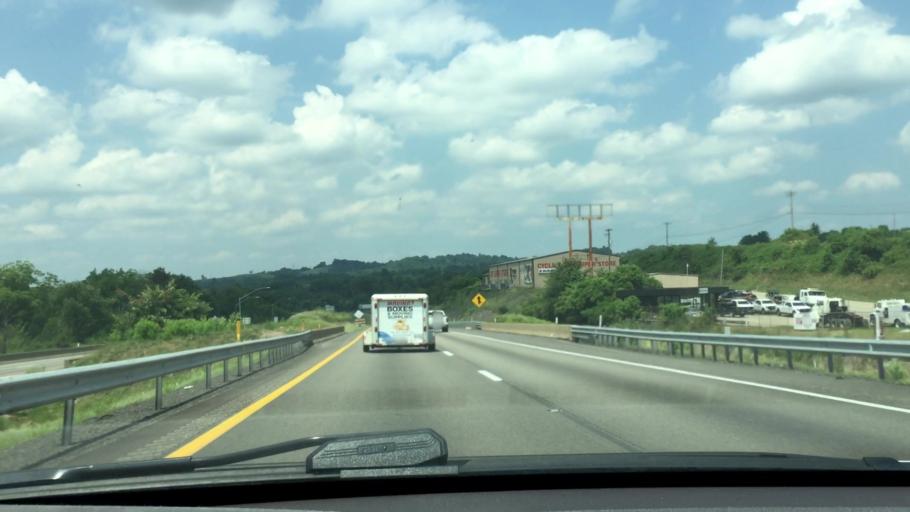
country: US
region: West Virginia
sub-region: Brooke County
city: Bethany
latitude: 40.1149
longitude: -80.4279
